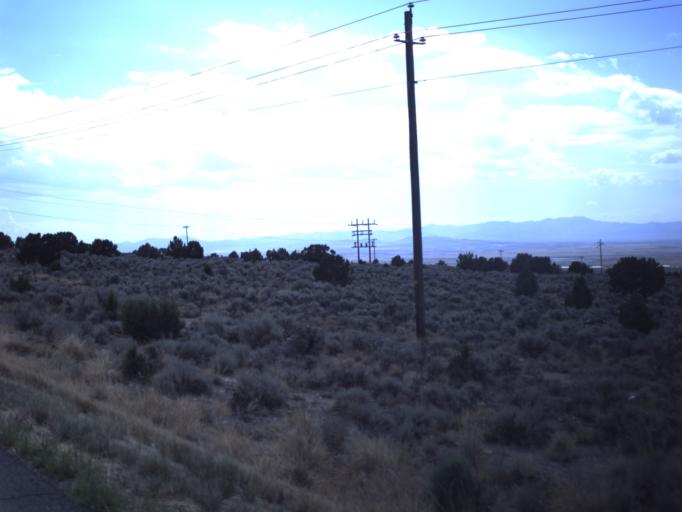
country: US
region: Utah
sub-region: Tooele County
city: Tooele
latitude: 40.3185
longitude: -112.2853
